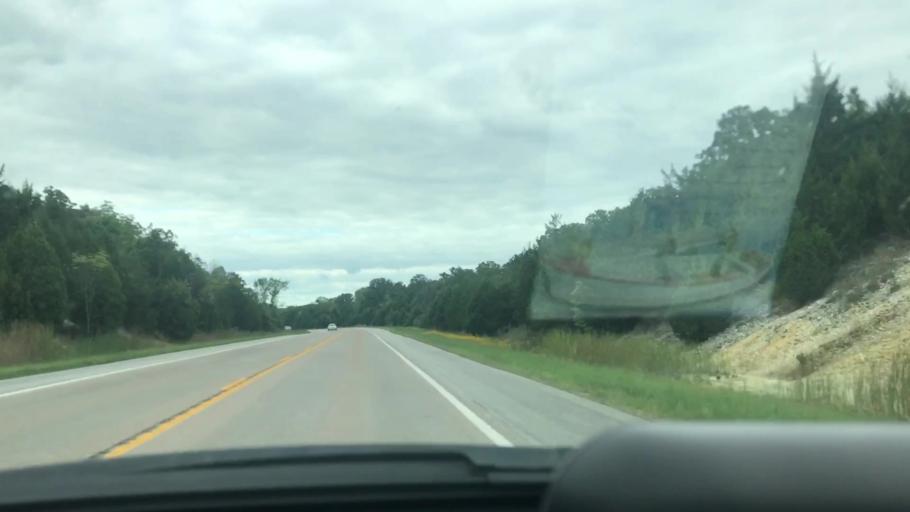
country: US
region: Missouri
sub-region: Benton County
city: Warsaw
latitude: 38.2015
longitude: -93.3259
